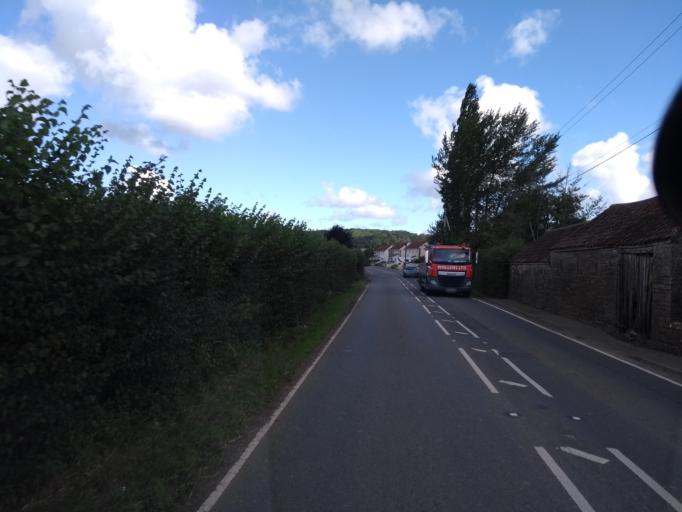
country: GB
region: England
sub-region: Somerset
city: Street
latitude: 51.0962
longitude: -2.7330
